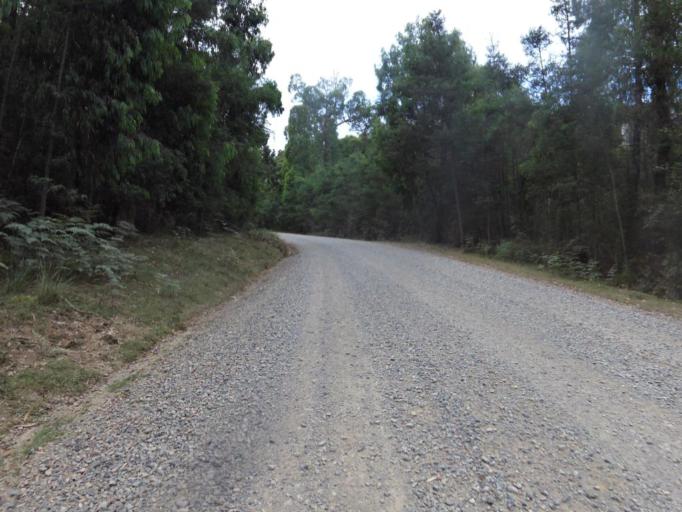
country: AU
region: Victoria
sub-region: Yarra Ranges
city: Healesville
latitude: -37.4180
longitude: 145.5647
